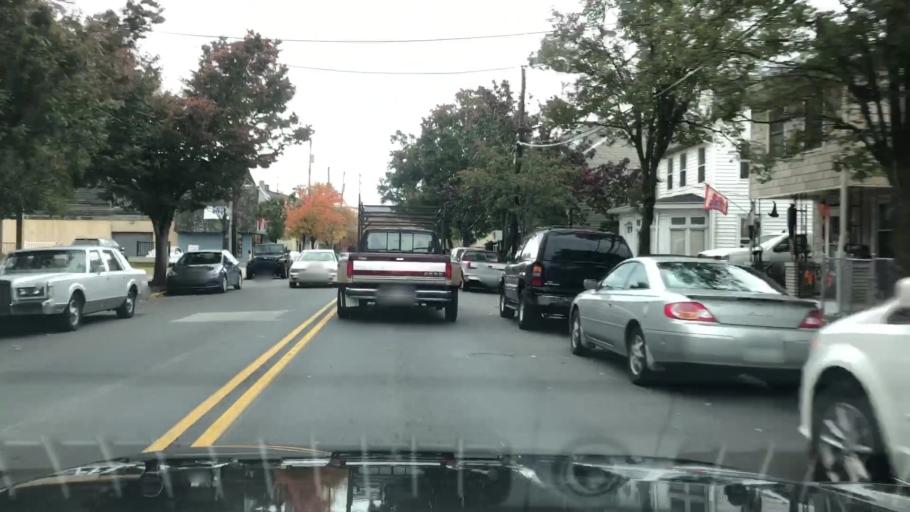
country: US
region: Pennsylvania
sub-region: Bucks County
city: Bristol
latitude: 40.0984
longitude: -74.8614
